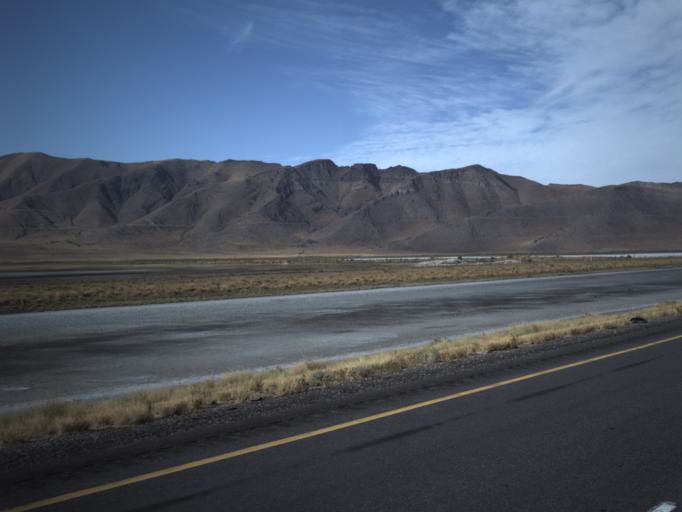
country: US
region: Utah
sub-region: Tooele County
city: Grantsville
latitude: 40.7222
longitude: -112.5602
